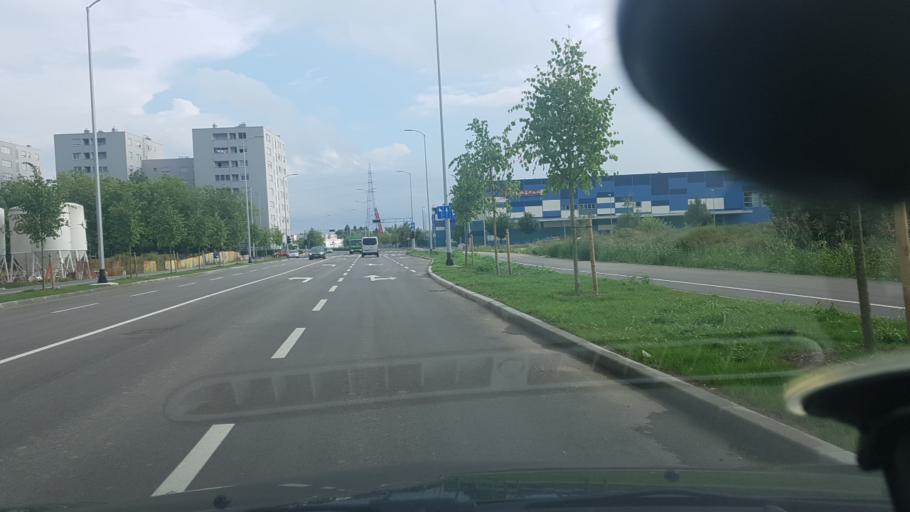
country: HR
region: Grad Zagreb
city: Stenjevec
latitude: 45.8015
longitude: 15.8861
